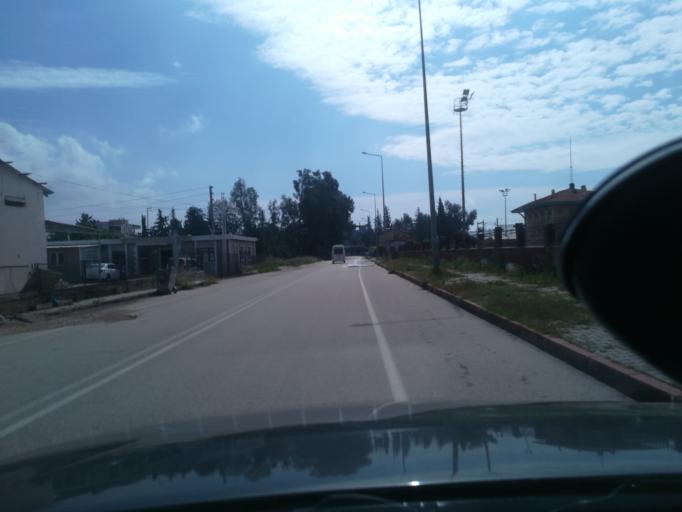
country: TR
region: Adana
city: Yuregir
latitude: 36.9845
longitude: 35.4342
